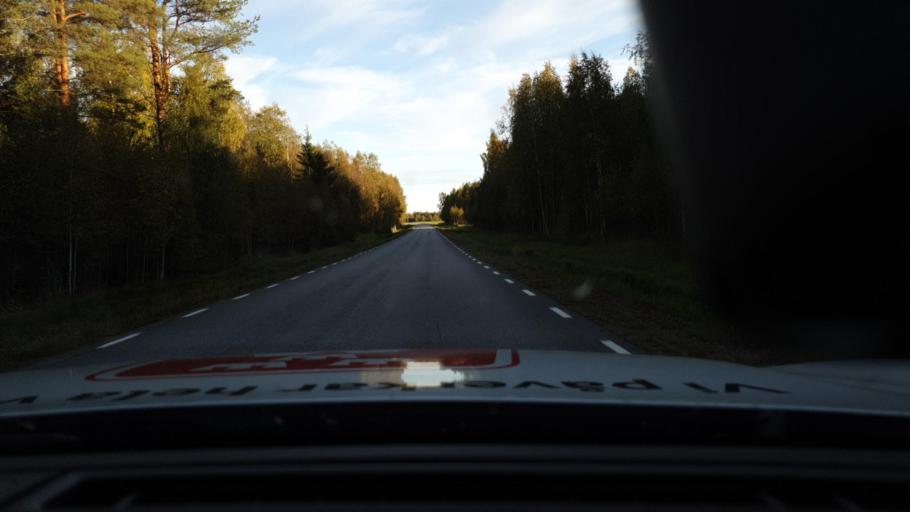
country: SE
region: Norrbotten
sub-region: Kalix Kommun
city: Toere
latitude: 65.8869
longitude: 22.6546
